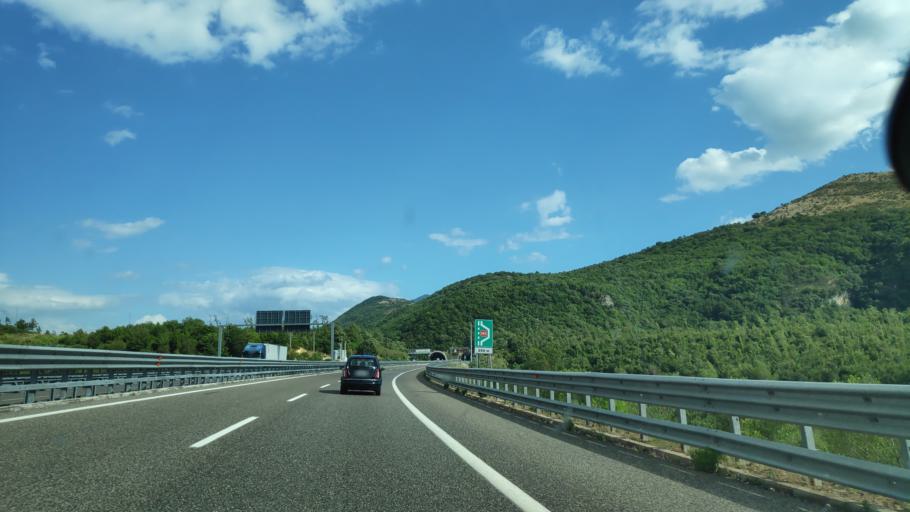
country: IT
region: Campania
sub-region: Provincia di Salerno
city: Sicignano degli Alburni
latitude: 40.6087
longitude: 15.2965
